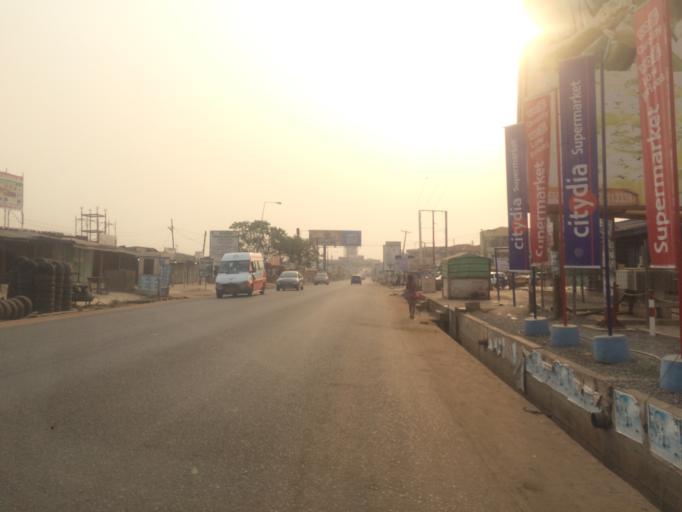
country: GH
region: Greater Accra
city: Nungua
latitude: 5.6260
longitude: -0.0828
